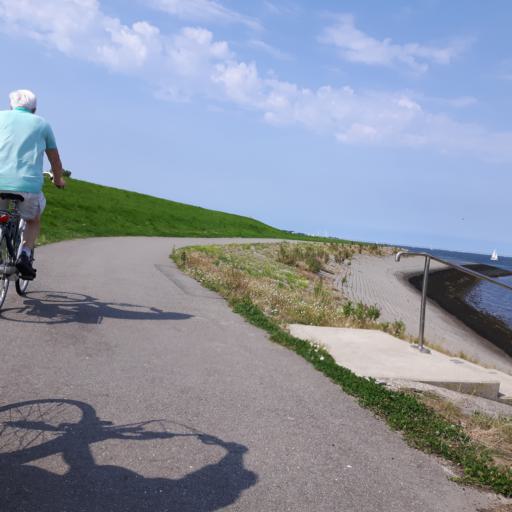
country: NL
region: Zeeland
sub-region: Gemeente Goes
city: Goes
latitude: 51.5422
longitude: 3.9281
